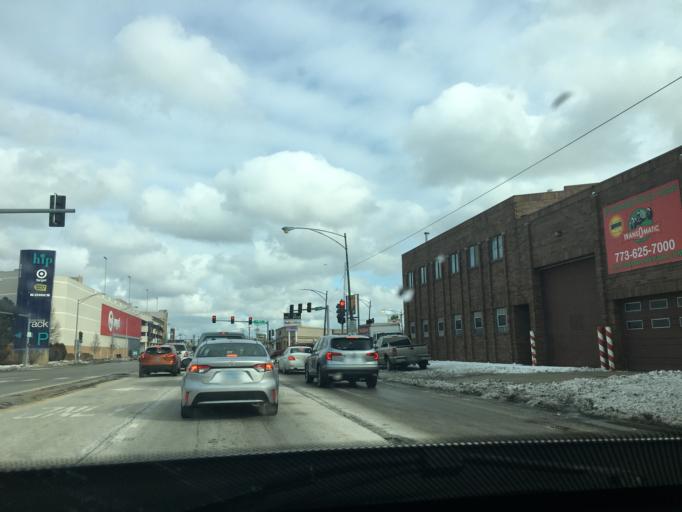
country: US
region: Illinois
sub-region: Cook County
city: Harwood Heights
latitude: 41.9524
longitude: -87.8103
